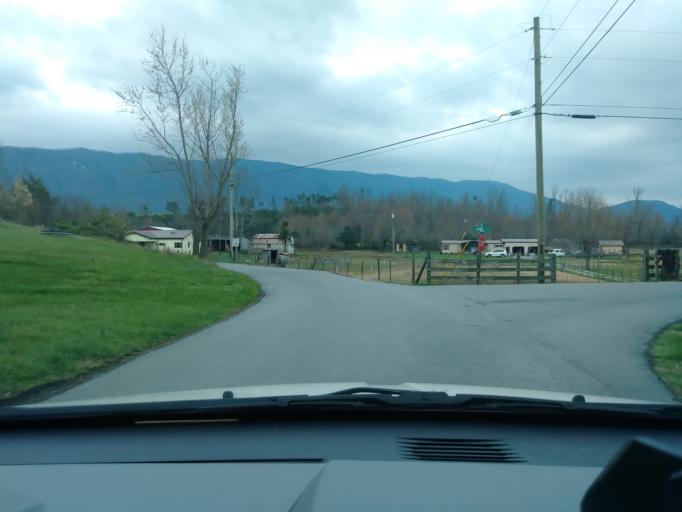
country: US
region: Tennessee
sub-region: Greene County
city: Tusculum
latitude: 36.0873
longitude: -82.7458
